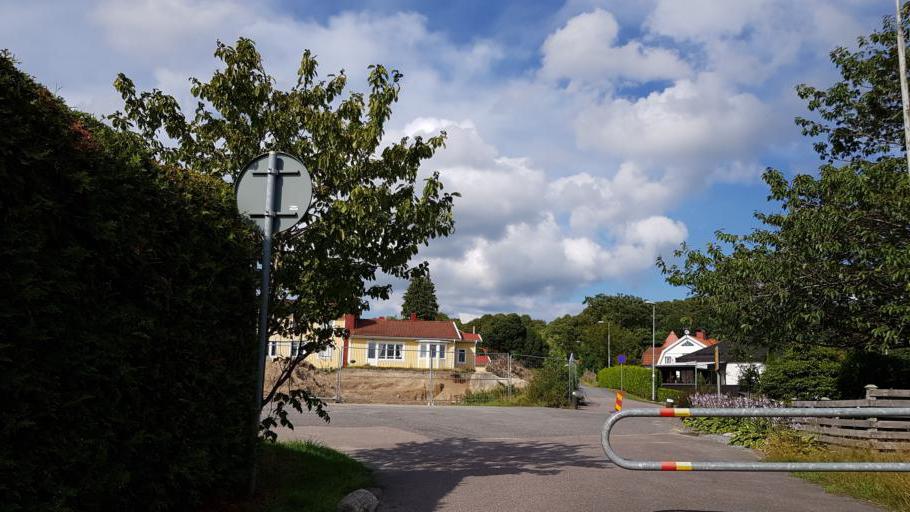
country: SE
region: Vaestra Goetaland
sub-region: Harryda Kommun
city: Molnlycke
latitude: 57.6613
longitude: 12.1185
